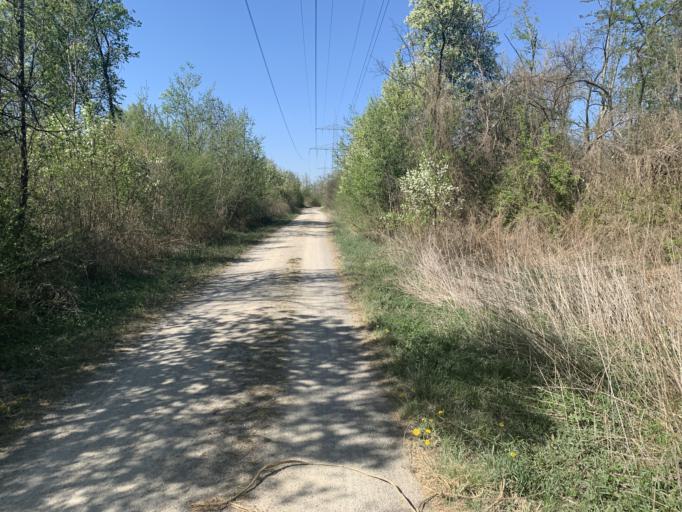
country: DE
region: Bavaria
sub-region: Swabia
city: Gersthofen
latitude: 48.4562
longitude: 10.8861
